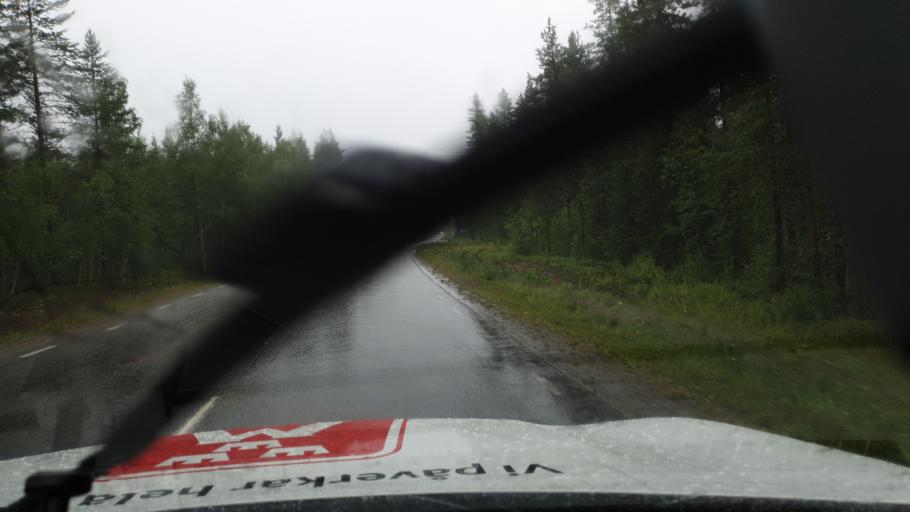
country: SE
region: Vaesterbotten
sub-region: Skelleftea Kommun
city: Langsele
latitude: 64.7969
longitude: 20.0142
